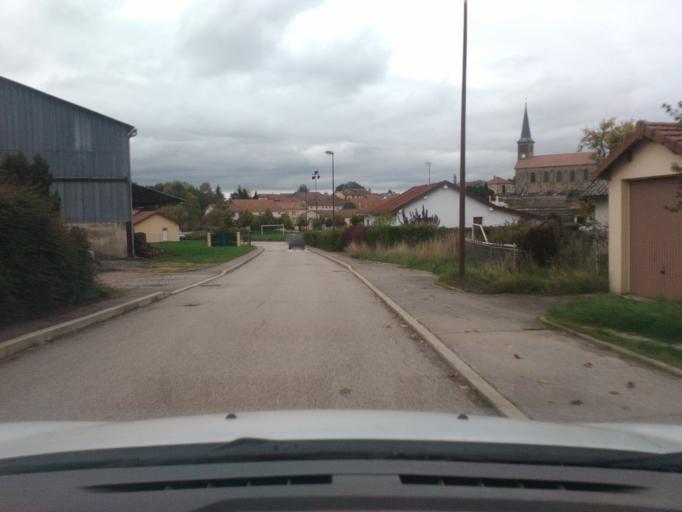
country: FR
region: Lorraine
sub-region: Departement des Vosges
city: Deyvillers
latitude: 48.1985
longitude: 6.4894
